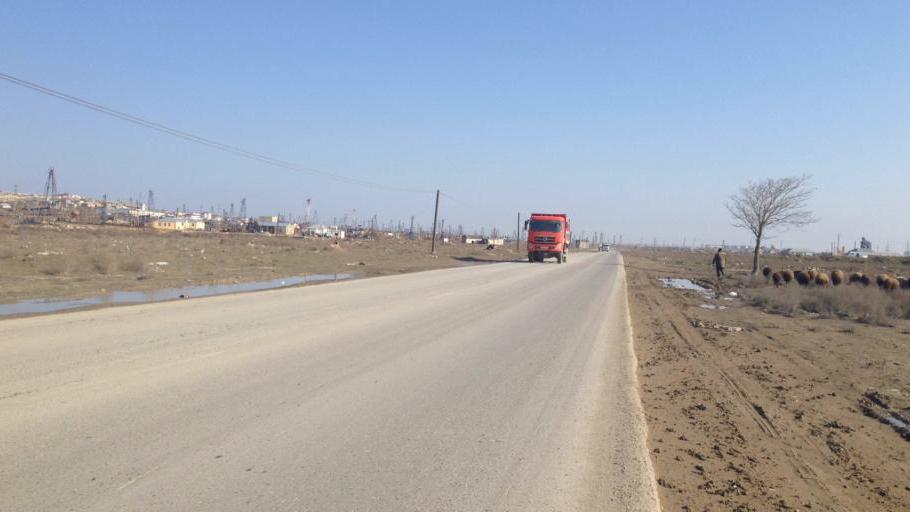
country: AZ
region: Baki
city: Balakhani
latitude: 40.4523
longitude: 49.8997
